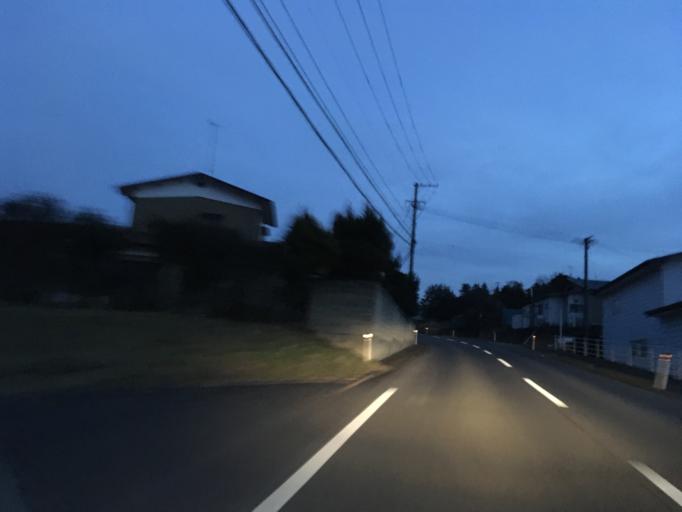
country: JP
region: Miyagi
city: Wakuya
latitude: 38.6975
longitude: 141.1616
